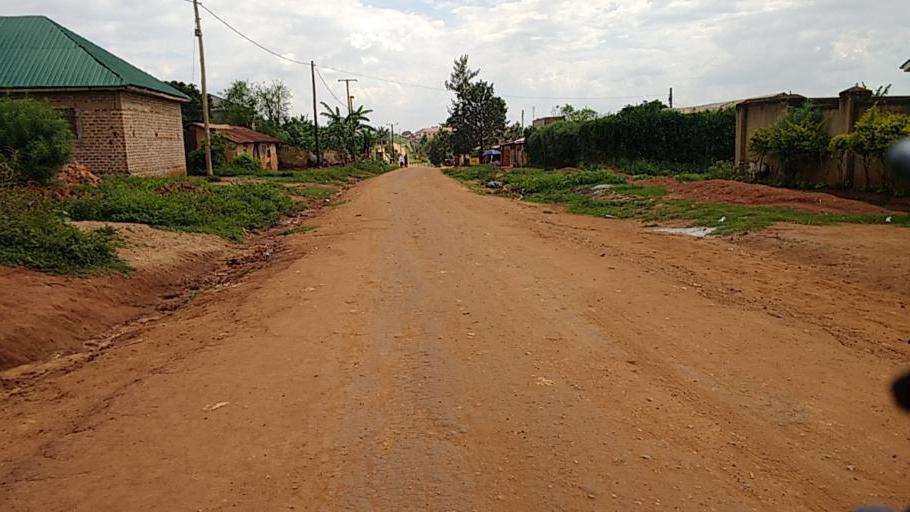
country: UG
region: Eastern Region
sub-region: Mbale District
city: Mbale
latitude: 1.0862
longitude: 34.1642
